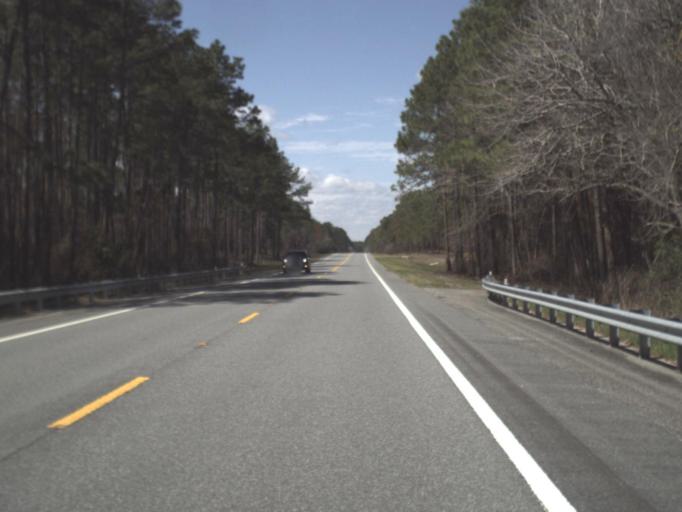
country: US
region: Florida
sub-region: Gadsden County
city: Midway
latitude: 30.3499
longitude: -84.5116
